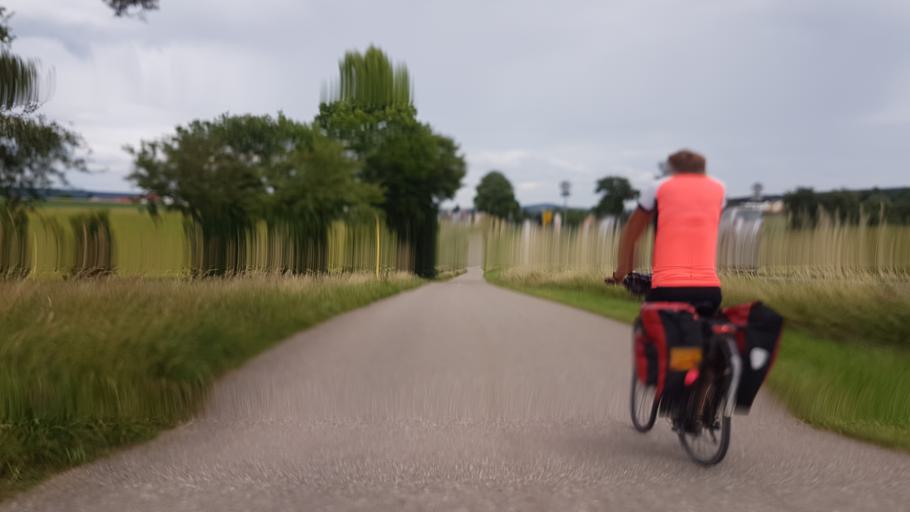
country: DE
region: Baden-Wuerttemberg
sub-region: Tuebingen Region
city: Obermarchtal
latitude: 48.2294
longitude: 9.5580
